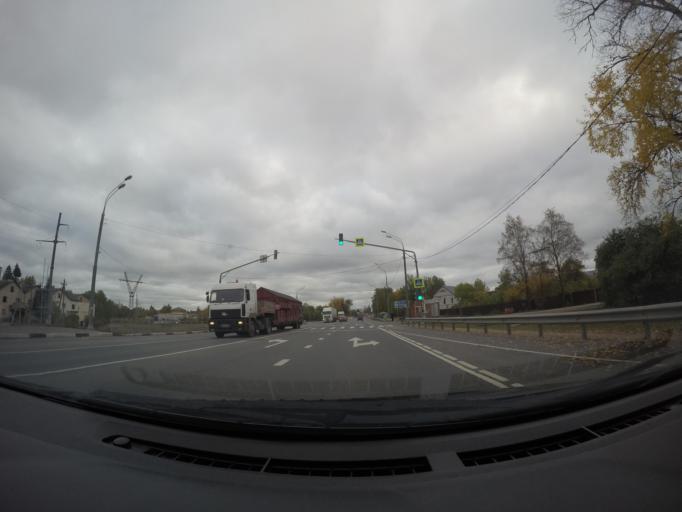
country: RU
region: Moskovskaya
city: Dorokhovo
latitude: 55.6263
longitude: 36.3397
